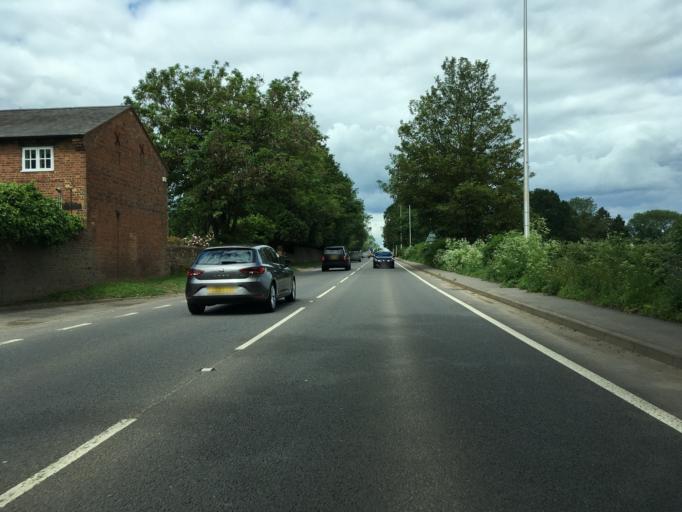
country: GB
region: England
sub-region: Northamptonshire
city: Towcester
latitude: 52.1201
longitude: -0.9686
